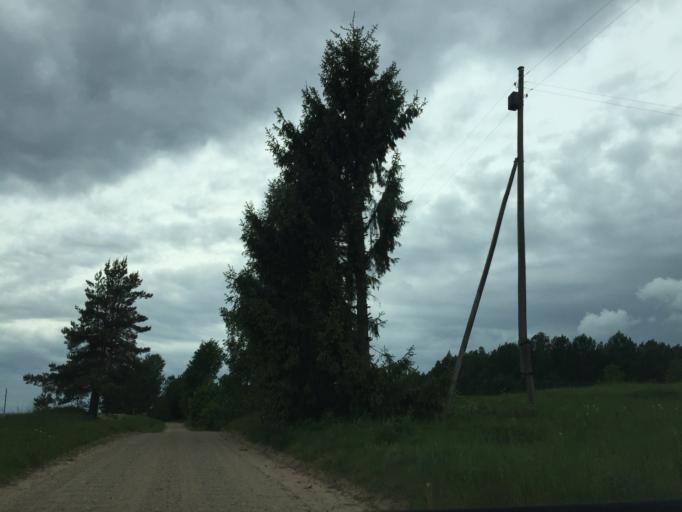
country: LV
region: Aglona
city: Aglona
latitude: 56.1635
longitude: 27.2466
